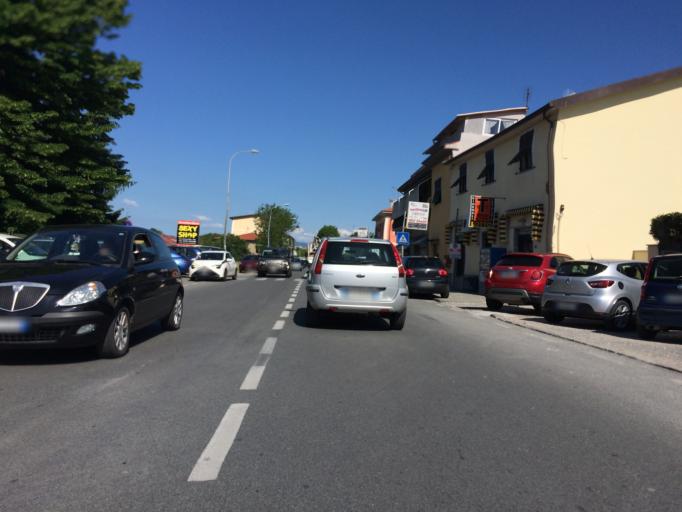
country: IT
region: Tuscany
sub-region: Provincia di Massa-Carrara
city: Borghetto-Melara
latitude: 44.0951
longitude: 9.9902
